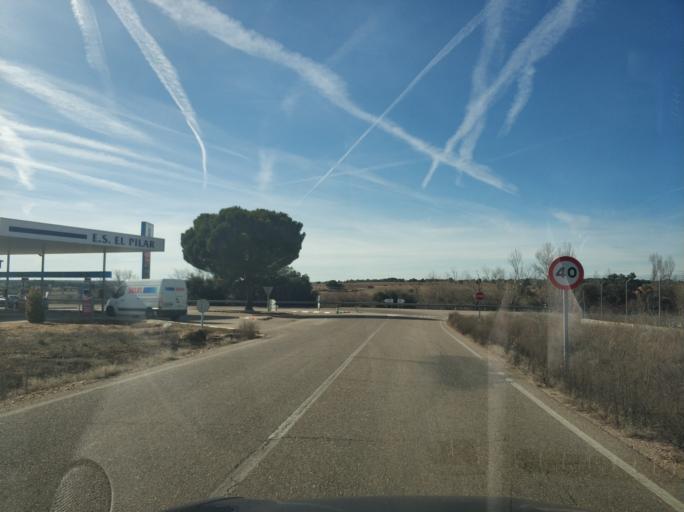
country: ES
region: Castille and Leon
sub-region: Provincia de Zamora
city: Cuelgamures
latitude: 41.2625
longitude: -5.7123
